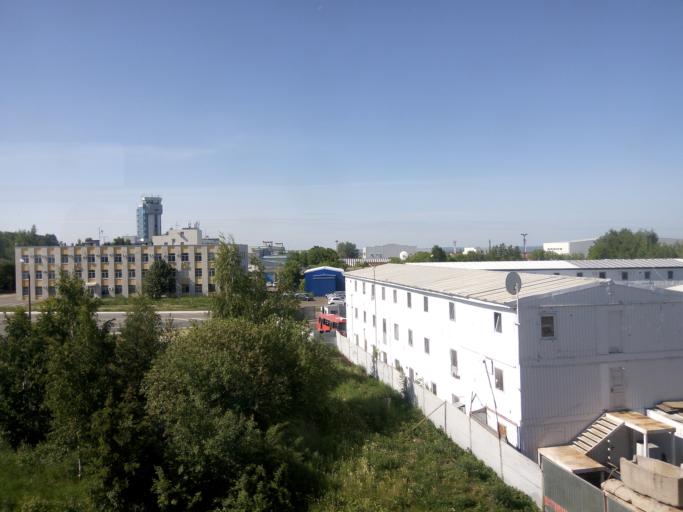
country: RU
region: Tatarstan
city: Stolbishchi
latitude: 55.6150
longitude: 49.2847
